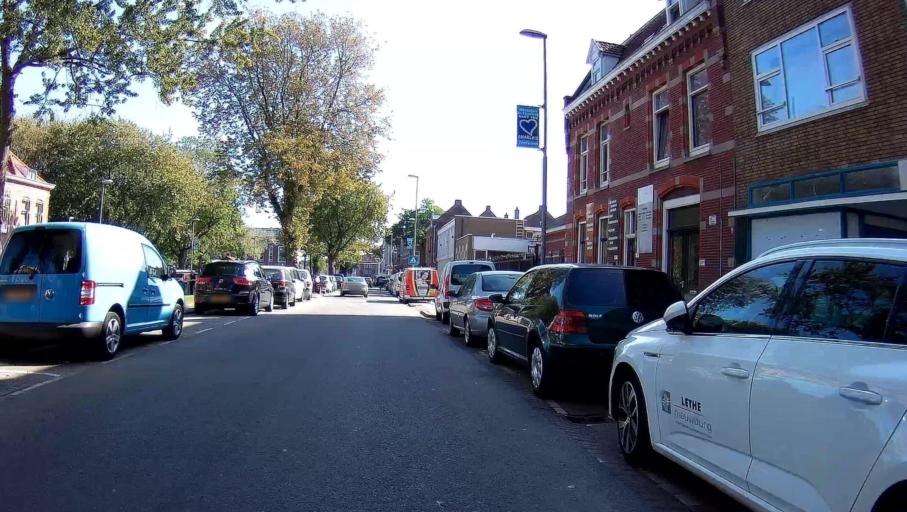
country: NL
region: South Holland
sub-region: Gemeente Rotterdam
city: Delfshaven
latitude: 51.8933
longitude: 4.4689
